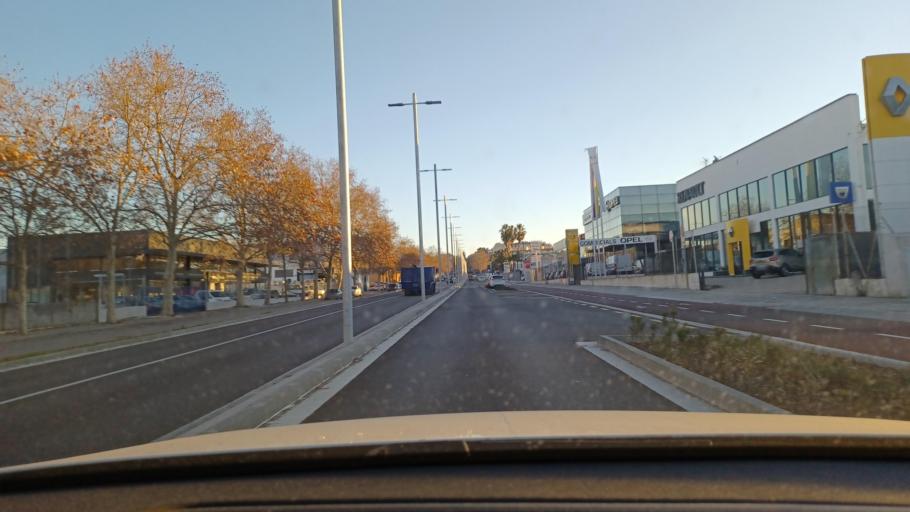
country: ES
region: Catalonia
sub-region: Provincia de Barcelona
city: Vilafranca del Penedes
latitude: 41.3355
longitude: 1.6855
